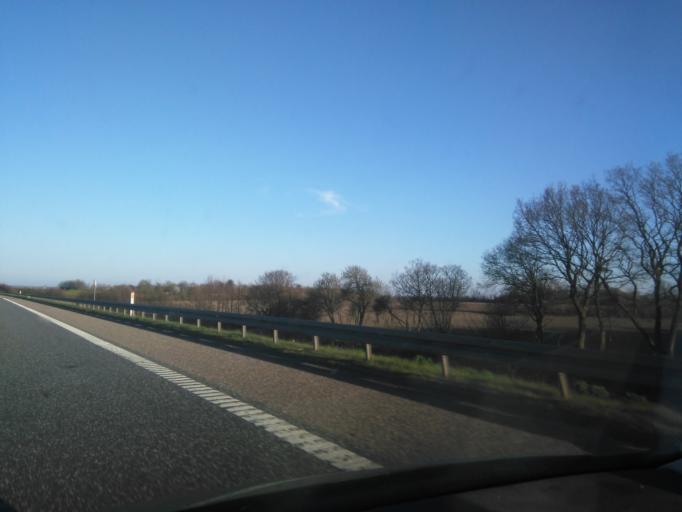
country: DK
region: Central Jutland
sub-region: Skanderborg Kommune
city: Galten
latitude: 56.1457
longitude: 9.8500
